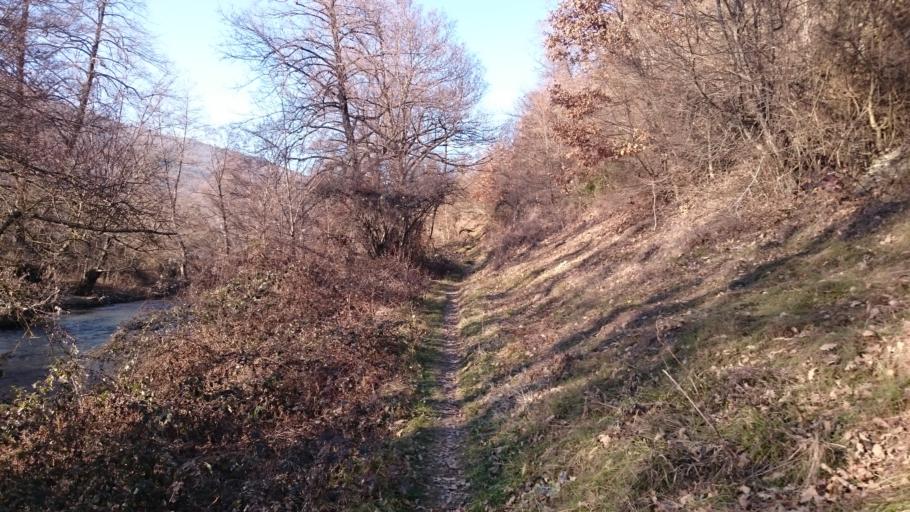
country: MK
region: Makedonski Brod
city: Makedonski Brod
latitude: 41.5124
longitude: 21.2251
